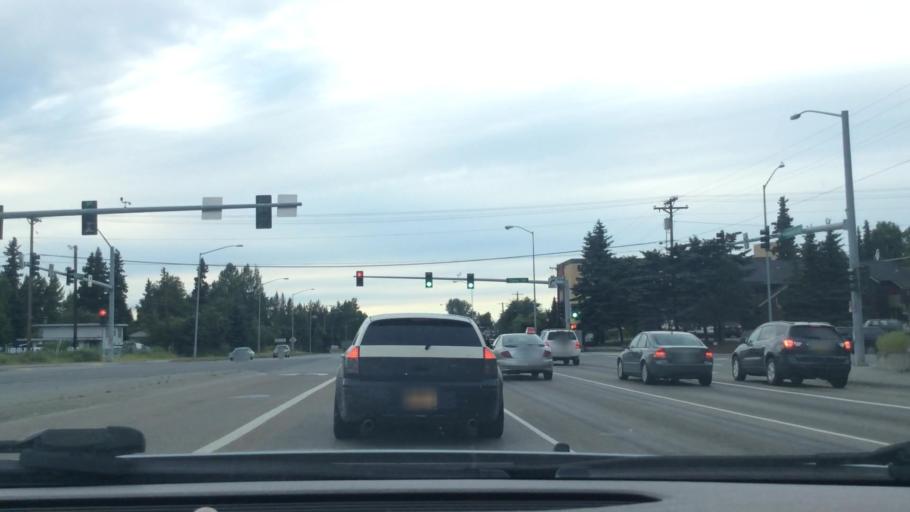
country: US
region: Alaska
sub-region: Anchorage Municipality
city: Anchorage
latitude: 61.1802
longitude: -149.9131
